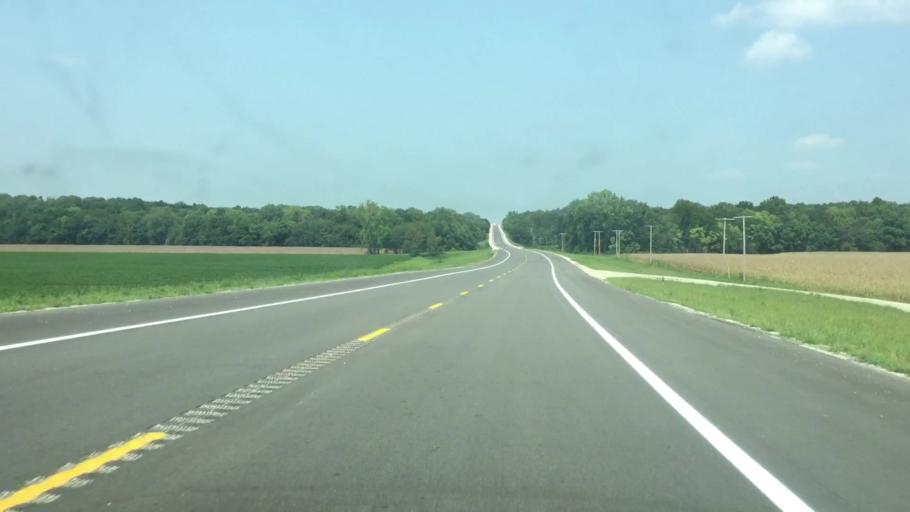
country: US
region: Kansas
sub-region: Anderson County
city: Garnett
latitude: 38.3363
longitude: -95.2489
